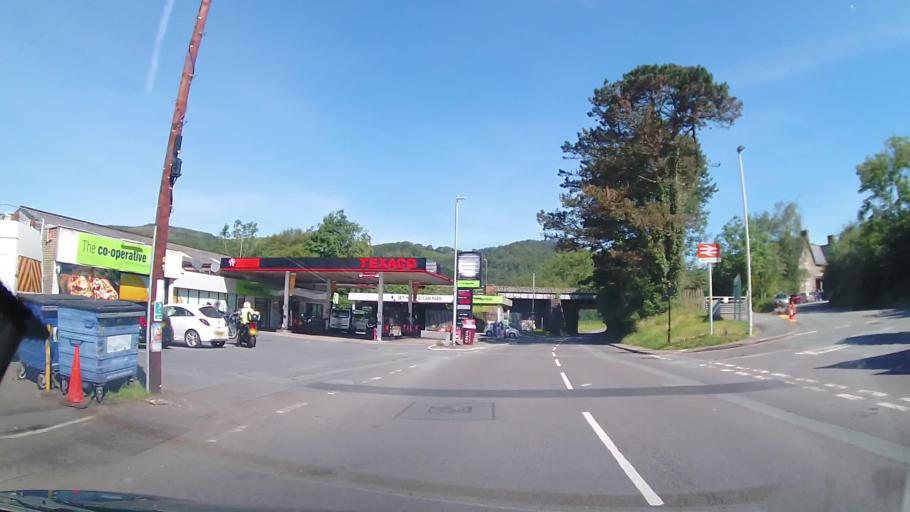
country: GB
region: Wales
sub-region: Sir Powys
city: Machynlleth
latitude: 52.5939
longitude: -3.8550
